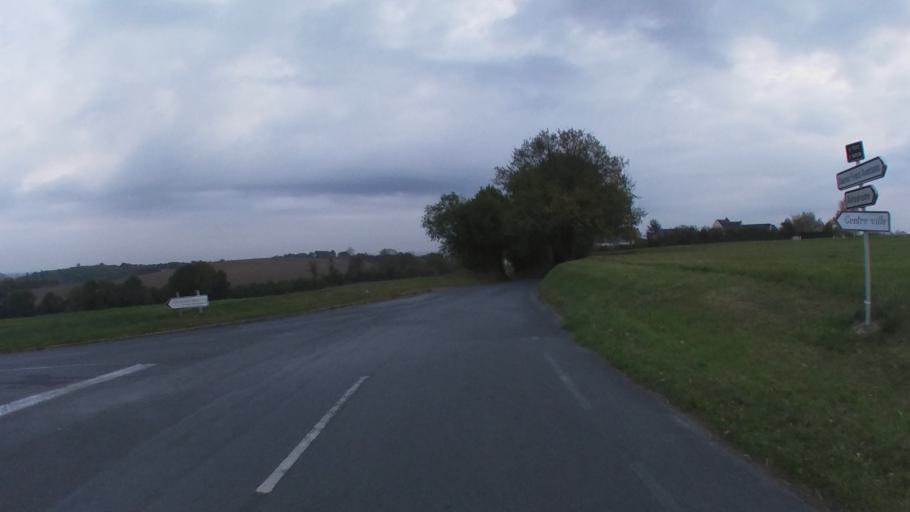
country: FR
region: Pays de la Loire
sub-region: Departement de Maine-et-Loire
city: Saumur
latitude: 47.2619
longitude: -0.1145
